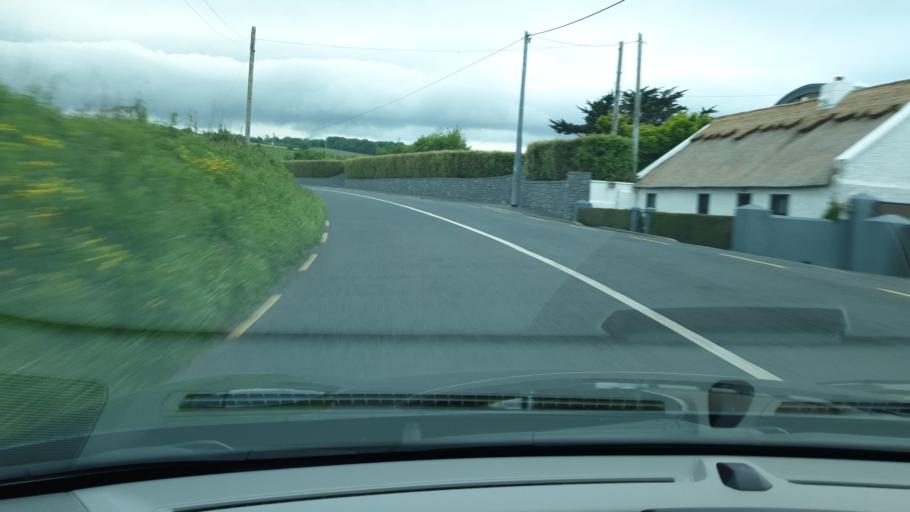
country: IE
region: Leinster
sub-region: Fingal County
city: Skerries
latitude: 53.5865
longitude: -6.1416
